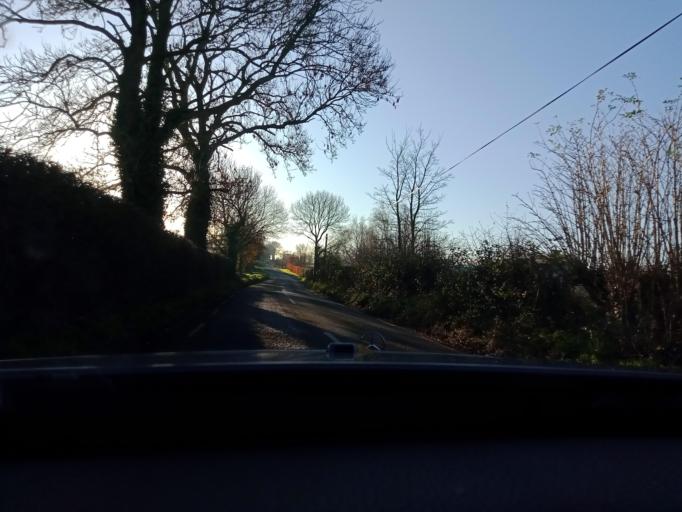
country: IE
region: Leinster
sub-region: Kilkenny
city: Callan
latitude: 52.5072
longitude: -7.3840
